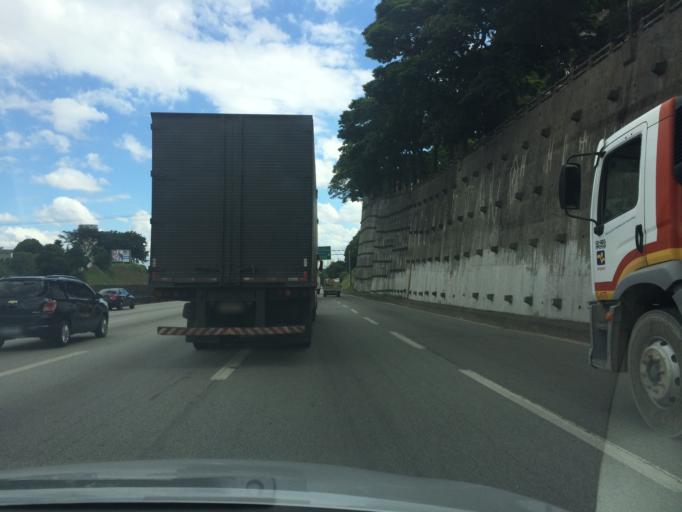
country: BR
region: Sao Paulo
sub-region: Guarulhos
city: Guarulhos
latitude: -23.4944
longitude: -46.5544
